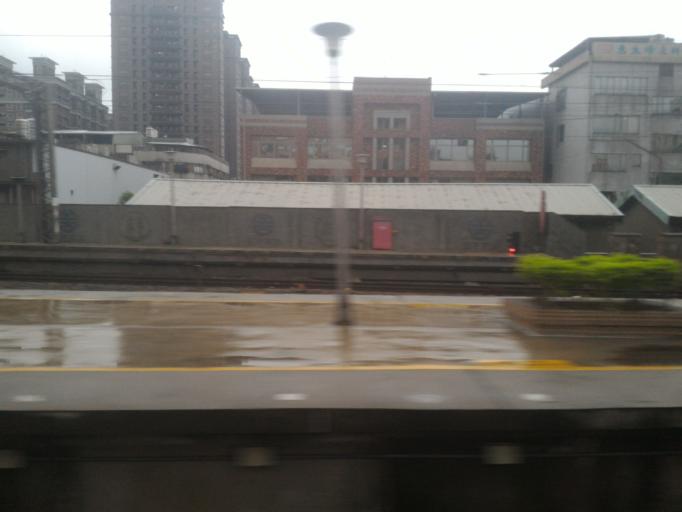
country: TW
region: Taipei
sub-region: Taipei
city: Banqiao
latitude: 24.9930
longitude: 121.4251
